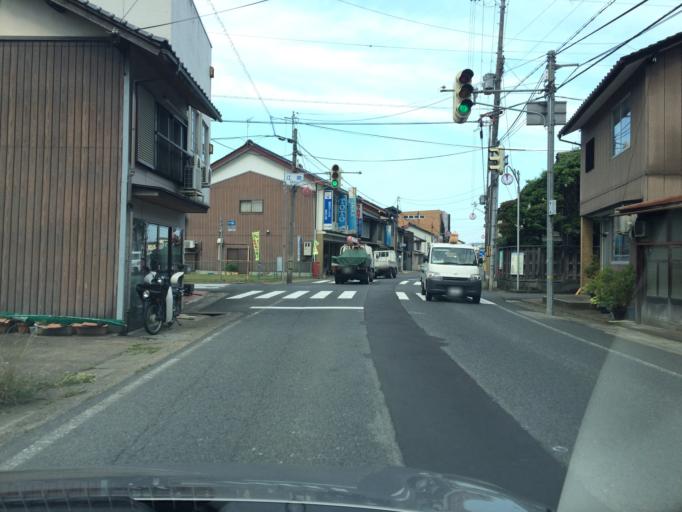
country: JP
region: Hyogo
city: Toyooka
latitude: 35.4667
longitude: 134.7756
